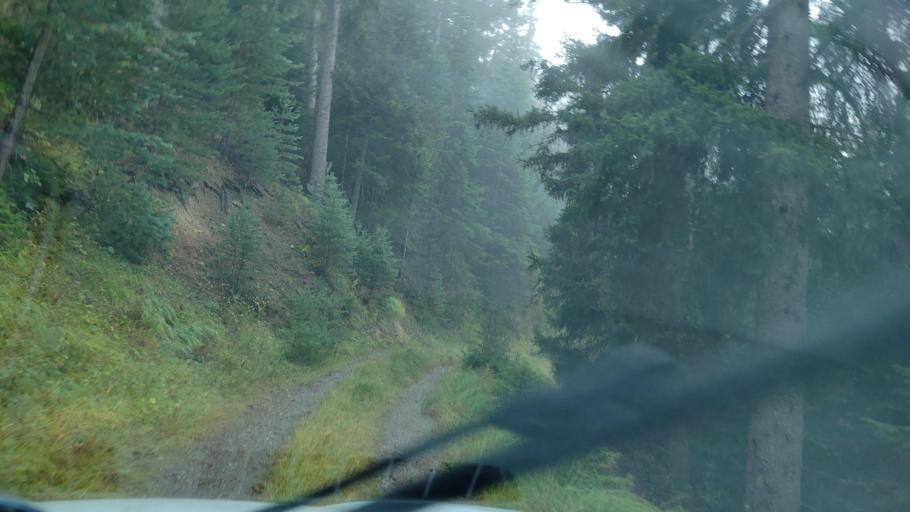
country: IT
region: Piedmont
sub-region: Provincia di Torino
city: Moncenisio
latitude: 45.2888
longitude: 6.8261
